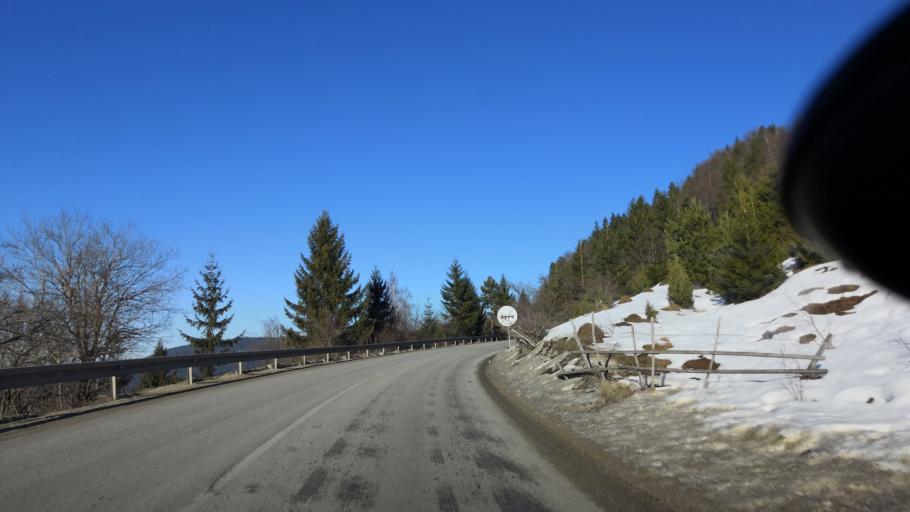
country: BA
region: Republika Srpska
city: Pale
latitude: 43.9052
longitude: 18.6366
